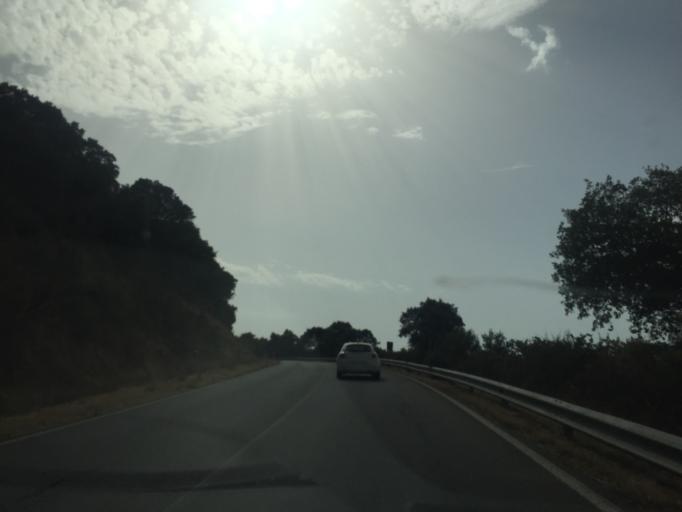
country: IT
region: Sardinia
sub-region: Provincia di Olbia-Tempio
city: Sant'Antonio di Gallura
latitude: 40.9789
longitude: 9.2589
